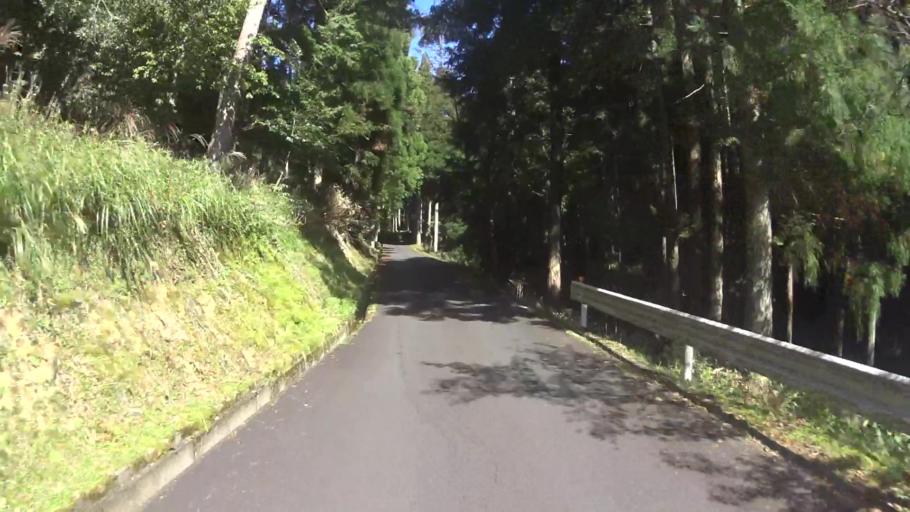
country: JP
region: Hyogo
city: Toyooka
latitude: 35.5433
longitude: 134.9583
